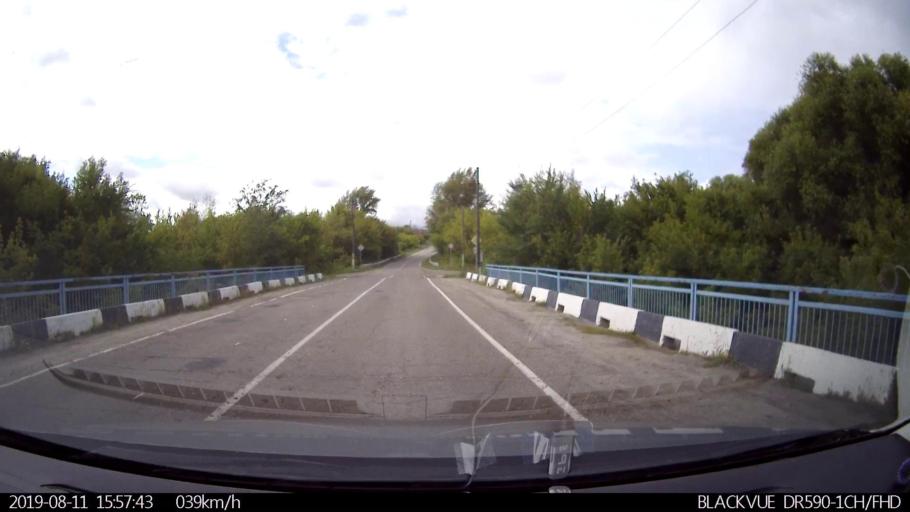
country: RU
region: Ulyanovsk
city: Ignatovka
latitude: 53.9522
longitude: 47.6514
